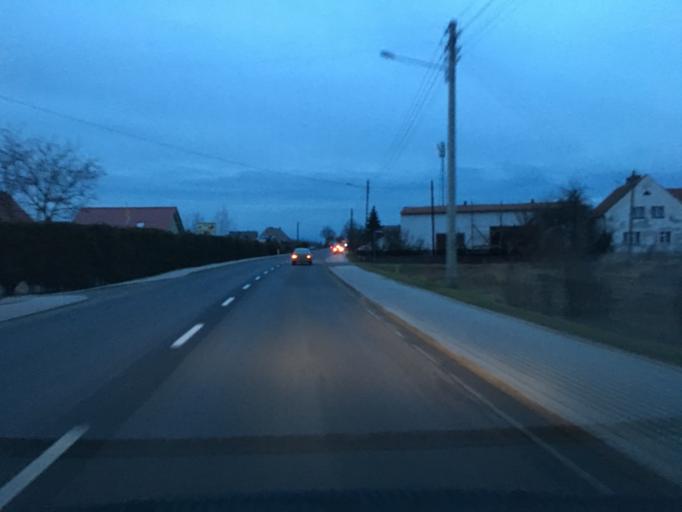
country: PL
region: Opole Voivodeship
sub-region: Powiat opolski
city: Dabrowa
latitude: 50.7044
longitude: 17.7830
